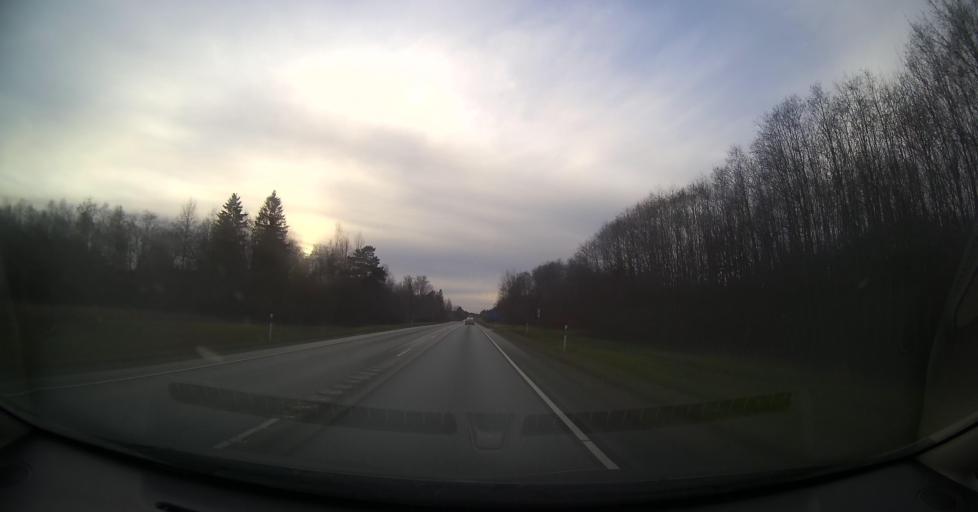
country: EE
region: Ida-Virumaa
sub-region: Johvi vald
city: Johvi
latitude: 59.3664
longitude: 27.4780
